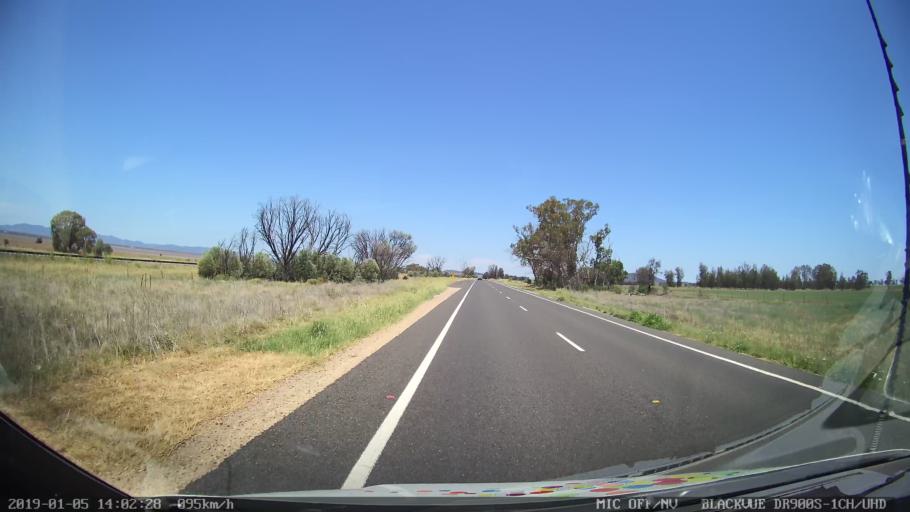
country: AU
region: New South Wales
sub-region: Gunnedah
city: Gunnedah
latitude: -31.1799
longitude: 150.3381
